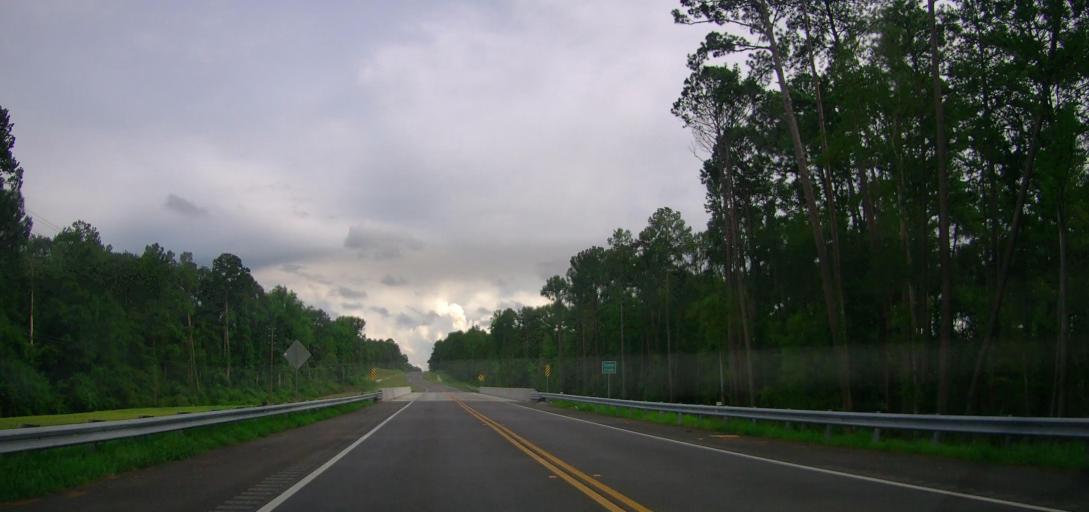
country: US
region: Georgia
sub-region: Wayne County
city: Jesup
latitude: 31.6699
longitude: -81.9187
